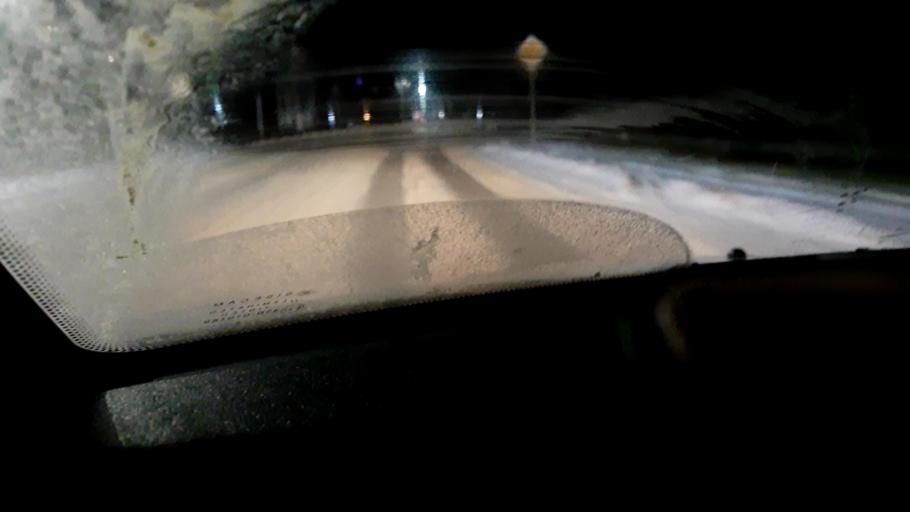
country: RU
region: Nizjnij Novgorod
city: Bogorodsk
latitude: 56.1031
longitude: 43.4732
